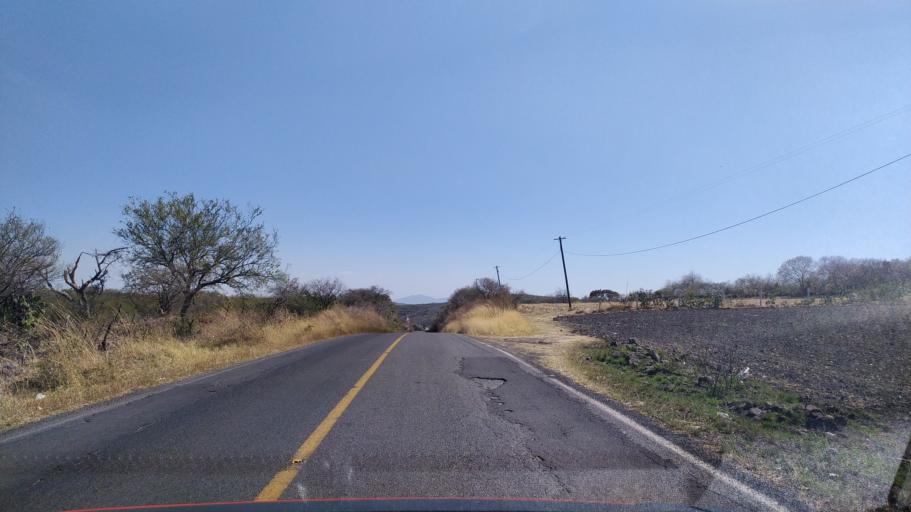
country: MX
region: Guanajuato
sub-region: Penjamo
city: Estacion la Piedad
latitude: 20.5030
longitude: -101.9756
